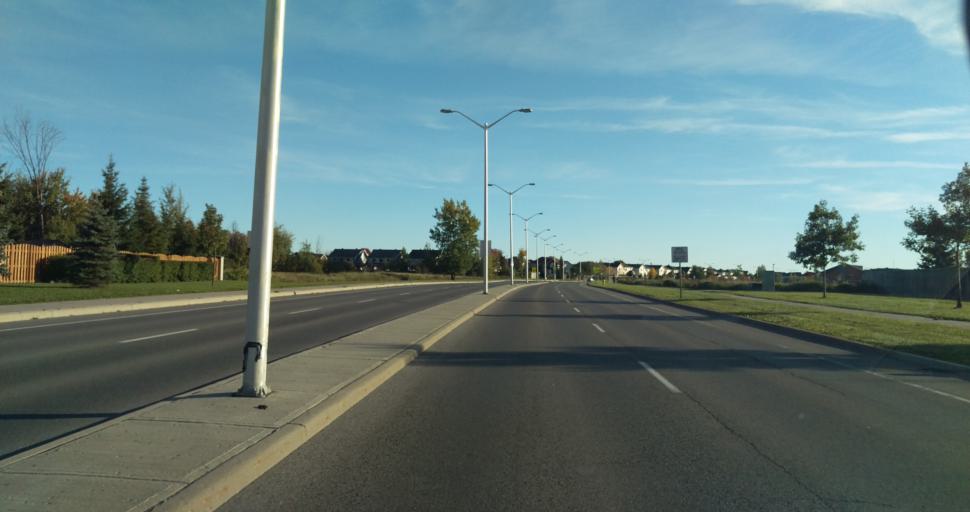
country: CA
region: Ontario
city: Clarence-Rockland
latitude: 45.4620
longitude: -75.4660
